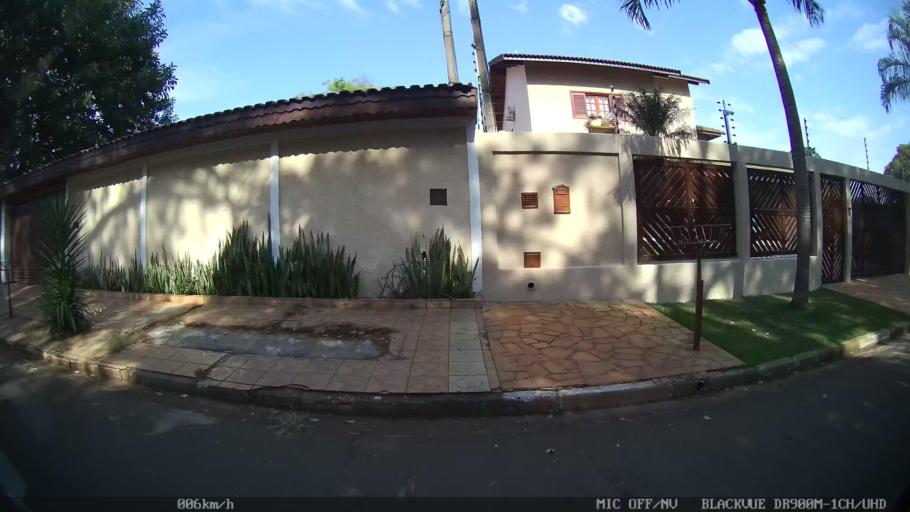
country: BR
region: Sao Paulo
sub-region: Paulinia
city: Paulinia
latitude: -22.7772
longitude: -47.1425
